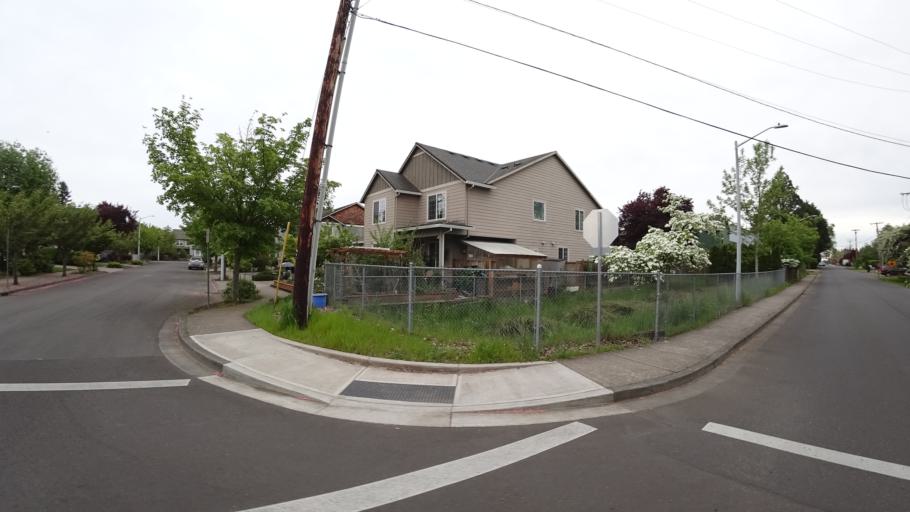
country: US
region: Oregon
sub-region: Washington County
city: Aloha
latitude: 45.5023
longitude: -122.9121
